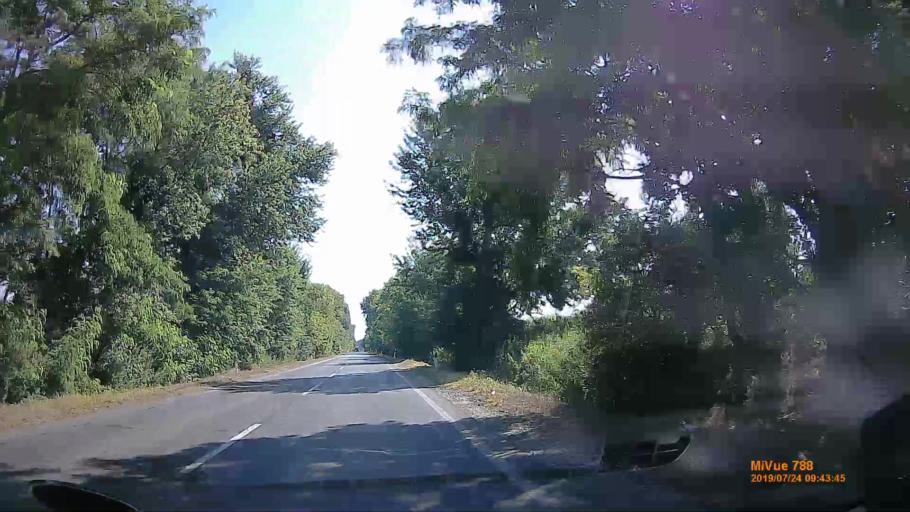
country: HU
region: Szabolcs-Szatmar-Bereg
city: Ofeherto
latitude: 47.9775
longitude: 22.0361
